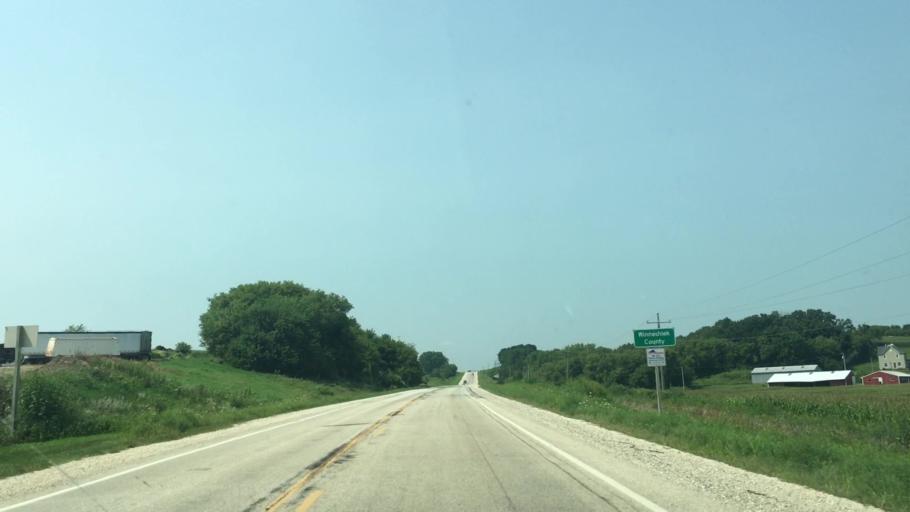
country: US
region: Iowa
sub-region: Fayette County
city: West Union
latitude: 43.0820
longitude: -91.8444
